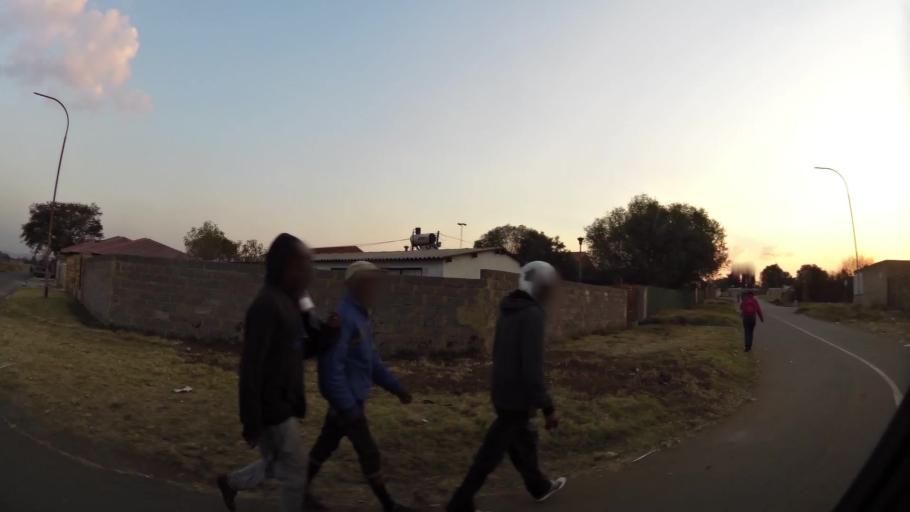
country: ZA
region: Gauteng
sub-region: City of Johannesburg Metropolitan Municipality
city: Soweto
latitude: -26.2860
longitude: 27.8826
